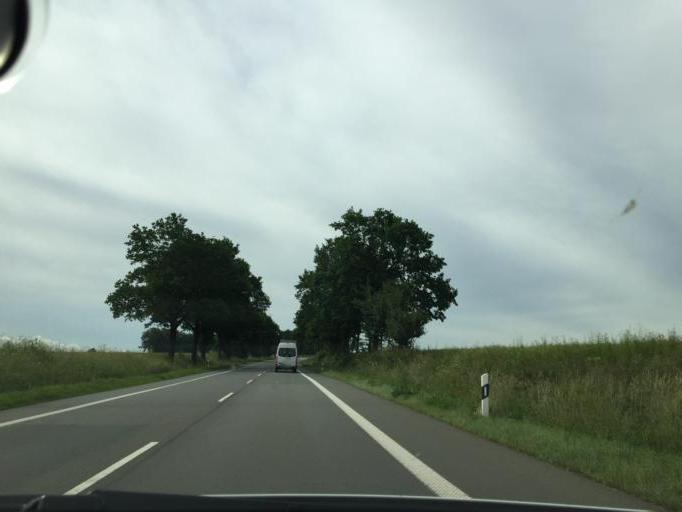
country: DE
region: North Rhine-Westphalia
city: Warburg
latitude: 51.5441
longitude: 9.1331
